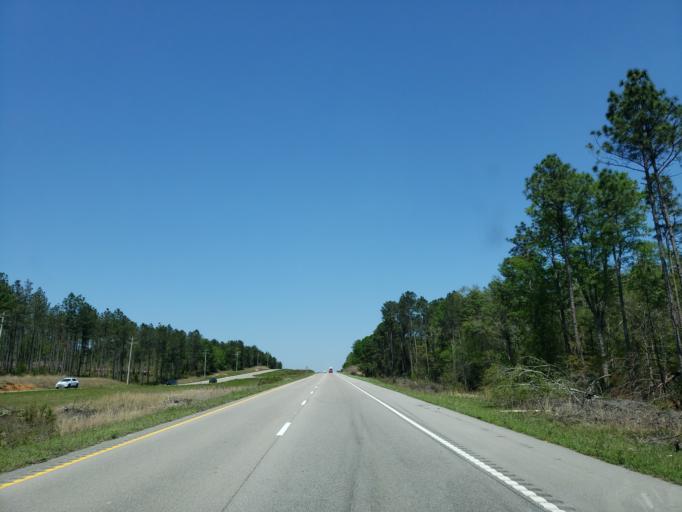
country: US
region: Mississippi
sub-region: Stone County
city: Wiggins
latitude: 30.9435
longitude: -89.1846
